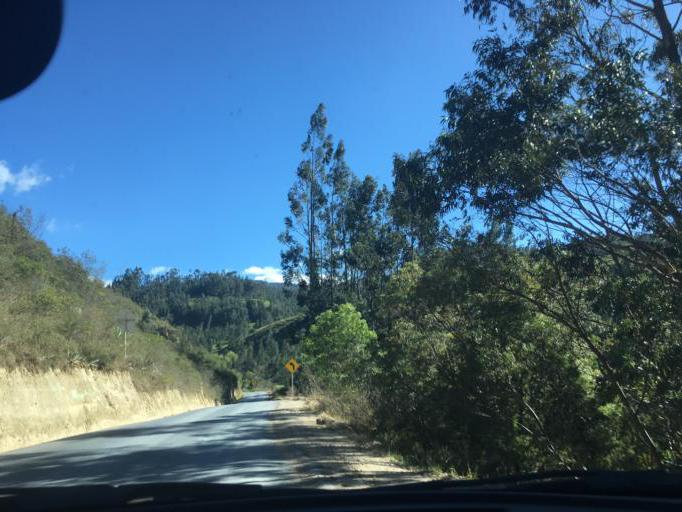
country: CO
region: Boyaca
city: Firavitoba
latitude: 5.5869
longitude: -72.9734
